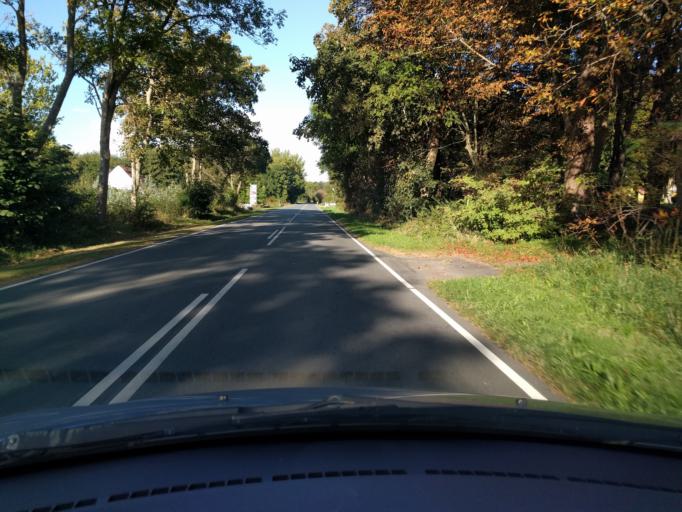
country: DK
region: South Denmark
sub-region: Assens Kommune
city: Assens
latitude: 55.2077
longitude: 9.9951
